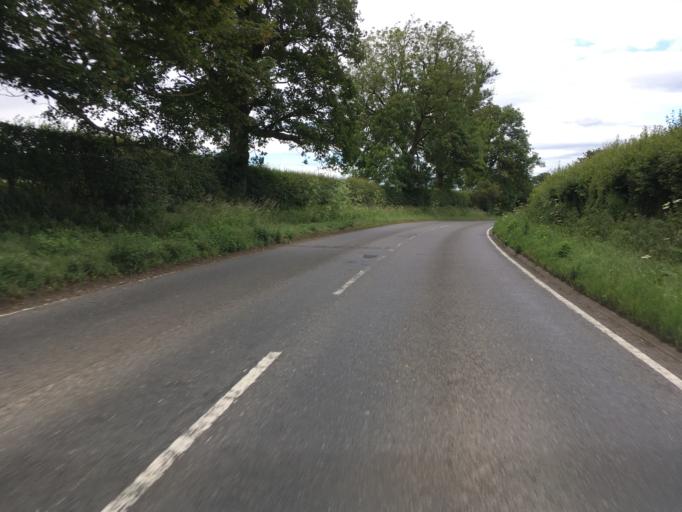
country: GB
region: England
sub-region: Central Bedfordshire
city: Woburn
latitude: 51.9743
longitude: -0.6410
